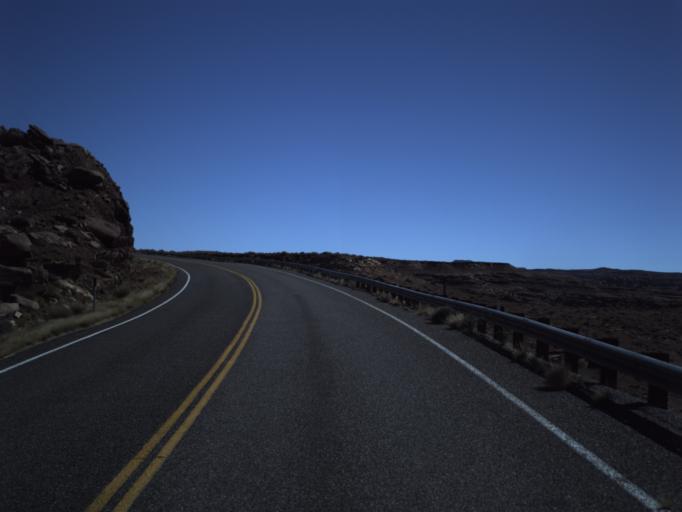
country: US
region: Utah
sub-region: San Juan County
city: Blanding
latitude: 37.8819
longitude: -110.4214
